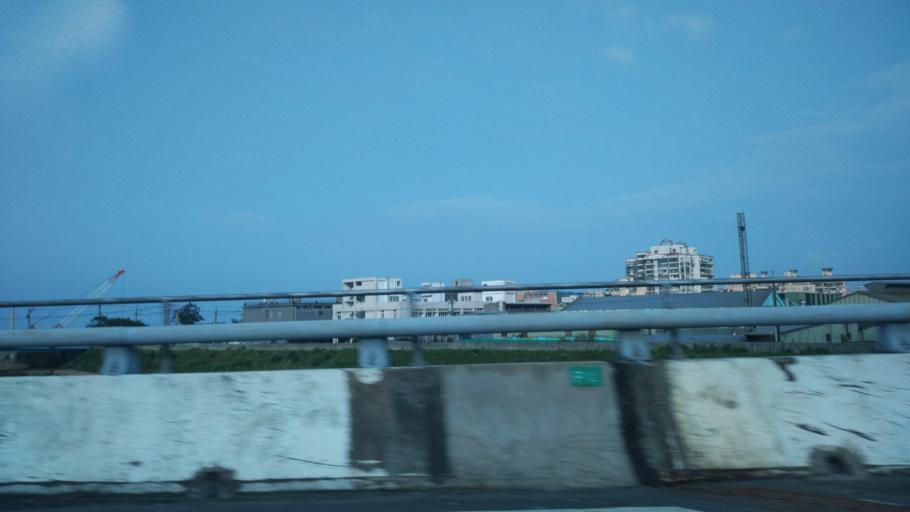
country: TW
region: Taiwan
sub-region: Keelung
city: Keelung
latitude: 25.2261
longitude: 121.6293
